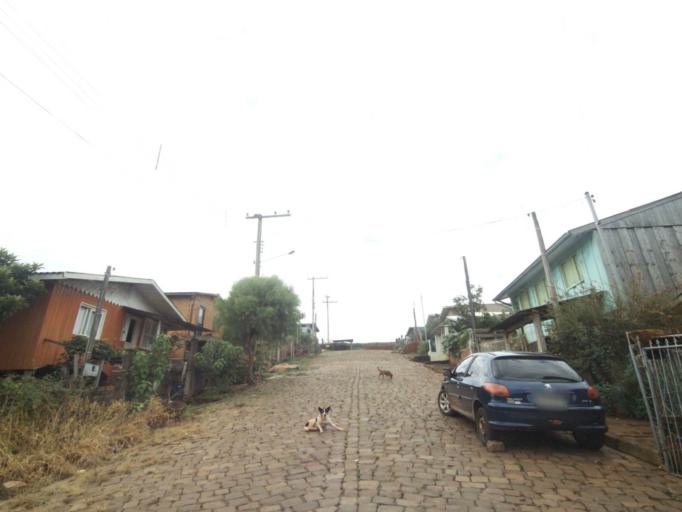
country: BR
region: Rio Grande do Sul
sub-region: Lagoa Vermelha
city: Lagoa Vermelha
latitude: -28.2232
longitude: -51.5243
